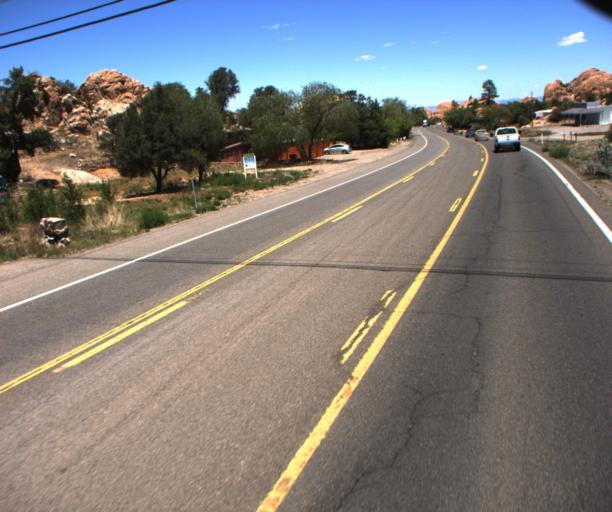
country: US
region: Arizona
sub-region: Yavapai County
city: Prescott
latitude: 34.5986
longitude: -112.4251
